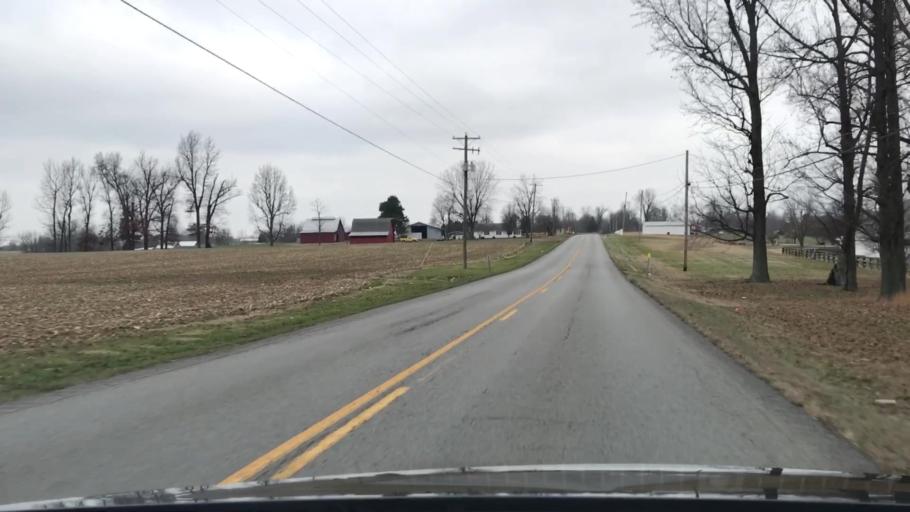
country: US
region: Kentucky
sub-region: McLean County
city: Calhoun
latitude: 37.3954
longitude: -87.2570
